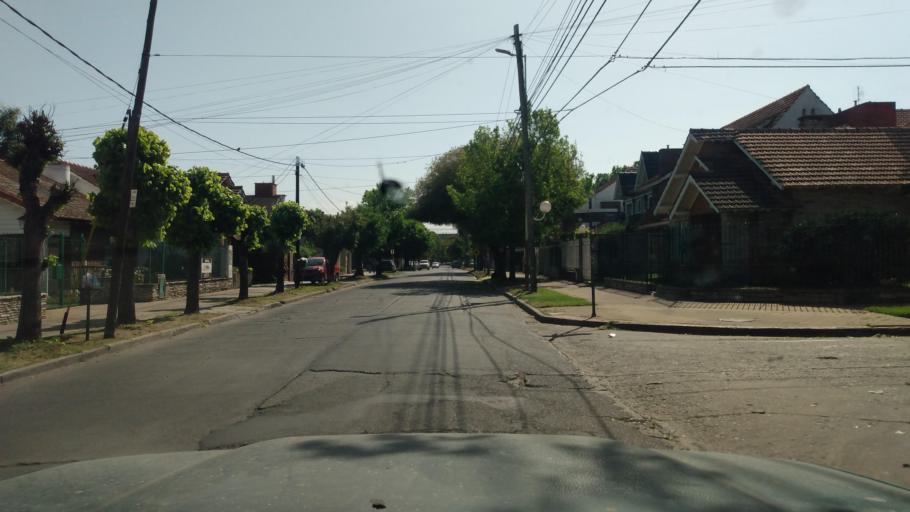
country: AR
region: Buenos Aires
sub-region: Partido de Moron
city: Moron
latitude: -34.6489
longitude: -58.5920
